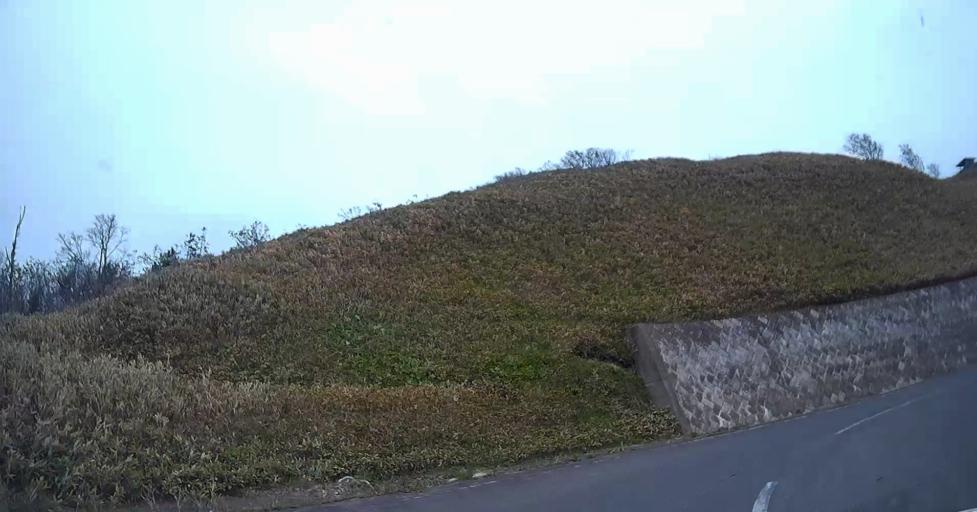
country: JP
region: Aomori
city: Shimokizukuri
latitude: 41.2143
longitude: 140.3553
